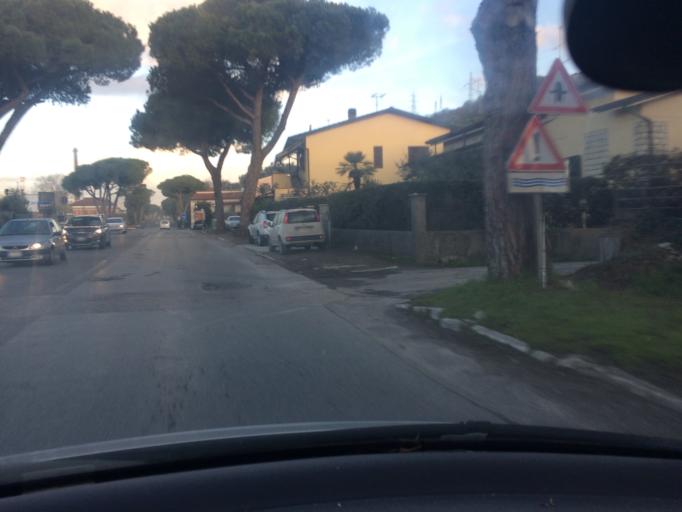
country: IT
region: Tuscany
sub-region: Provincia di Massa-Carrara
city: Carrara
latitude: 44.0417
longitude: 10.0904
